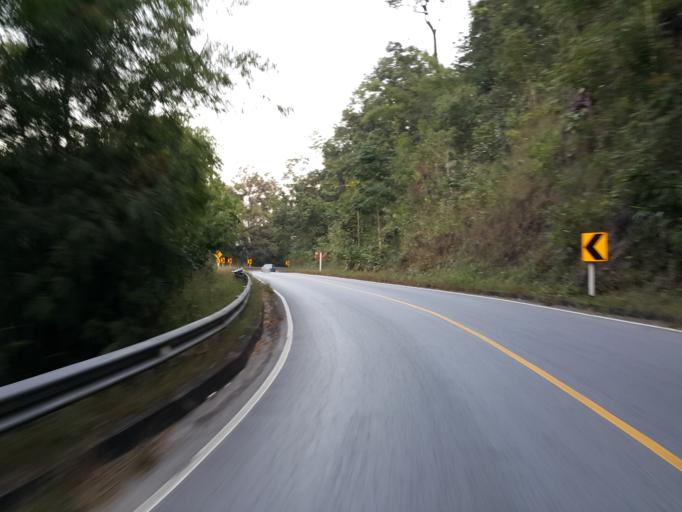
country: TH
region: Lampang
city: Thoen
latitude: 17.6825
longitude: 99.0827
